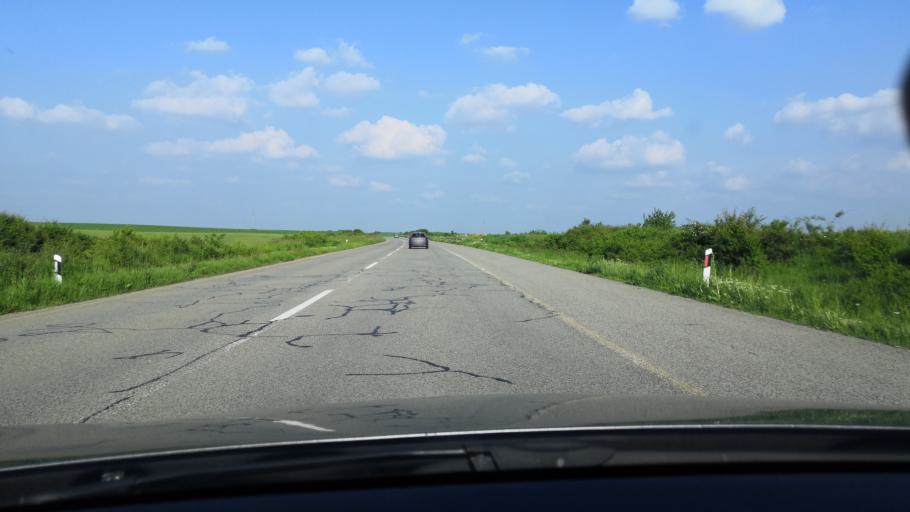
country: RS
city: Beska
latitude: 45.0907
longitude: 20.0467
